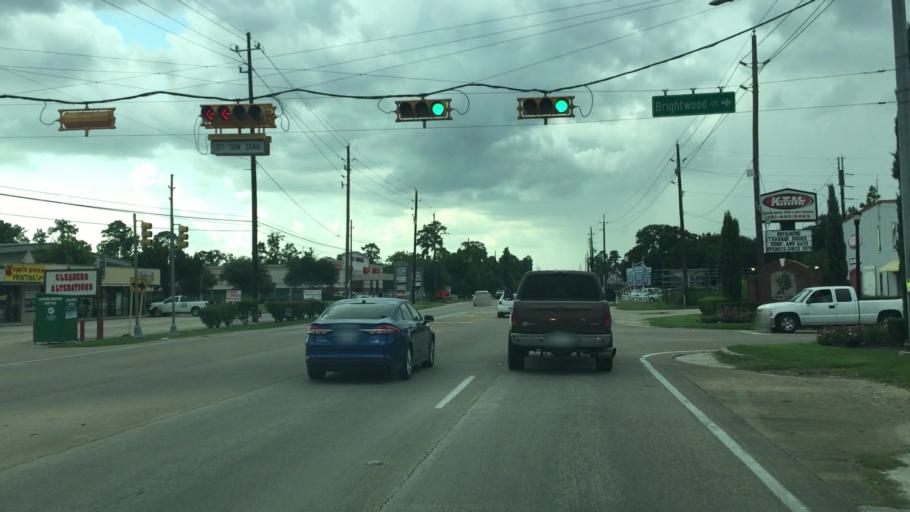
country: US
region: Texas
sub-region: Harris County
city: Hudson
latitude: 29.9989
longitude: -95.5063
